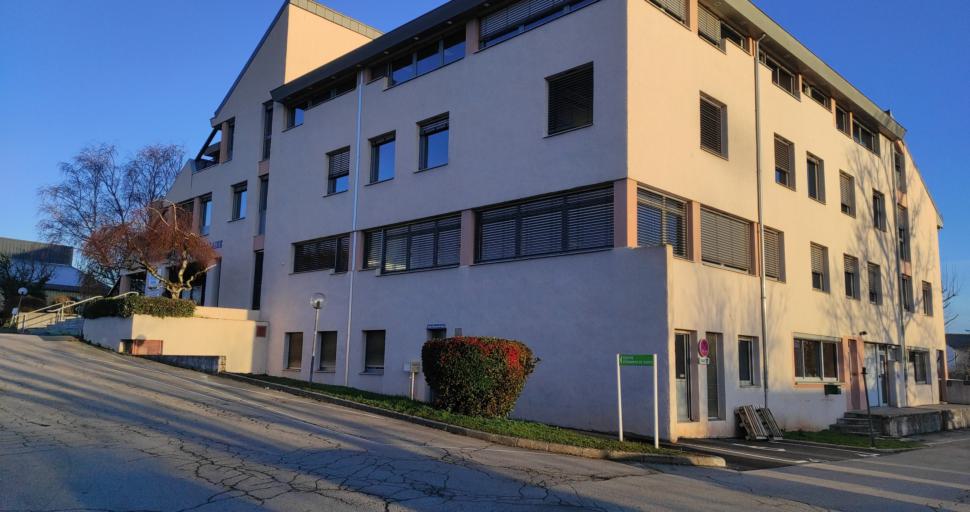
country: FR
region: Midi-Pyrenees
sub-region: Departement de l'Aveyron
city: Rodez
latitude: 44.3600
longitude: 2.5912
